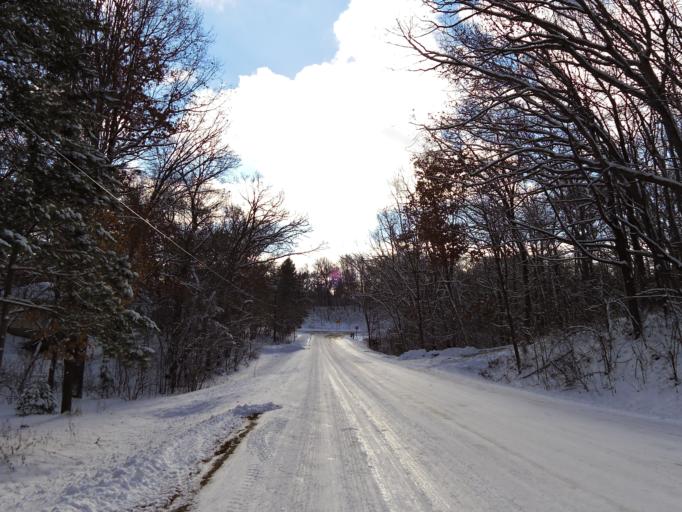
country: US
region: Minnesota
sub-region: Washington County
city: Lake Elmo
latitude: 44.9652
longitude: -92.8367
